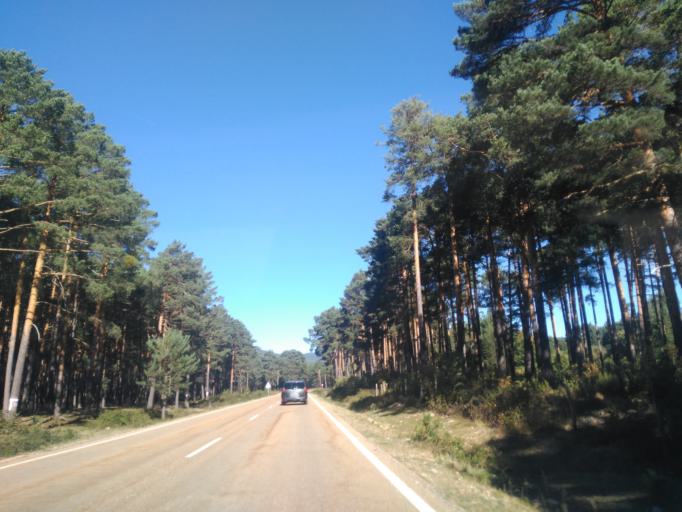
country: ES
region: Castille and Leon
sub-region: Provincia de Soria
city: Vinuesa
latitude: 41.9690
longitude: -2.7841
